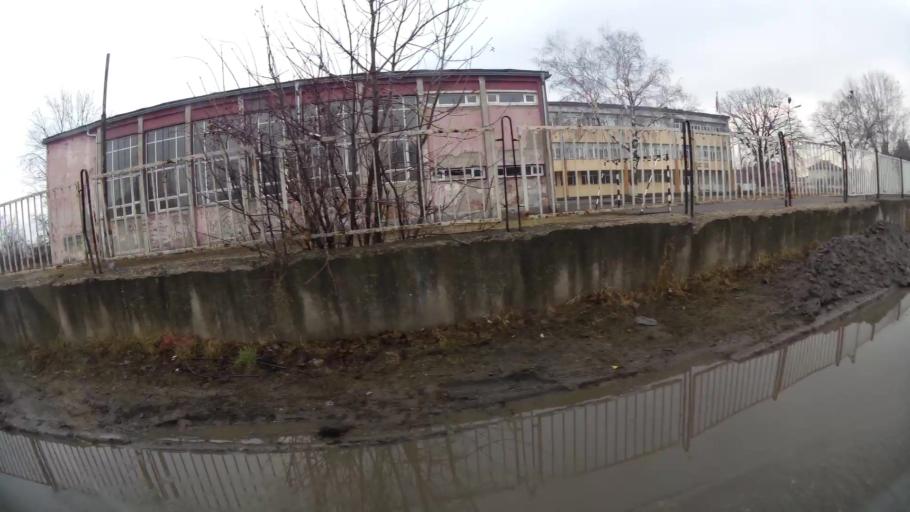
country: BG
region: Sofia-Capital
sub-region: Stolichna Obshtina
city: Sofia
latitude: 42.7418
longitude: 23.3437
